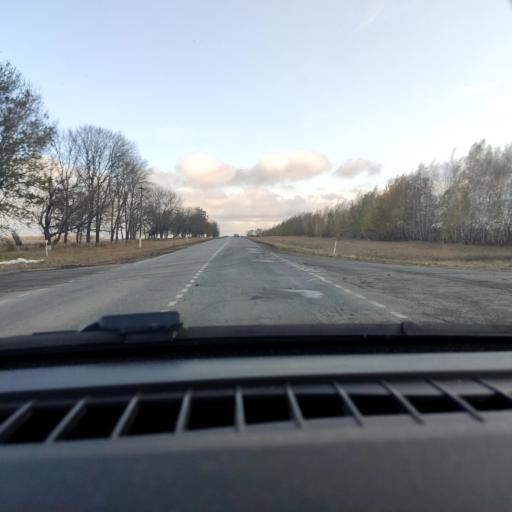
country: RU
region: Belgorod
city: Ilovka
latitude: 50.7134
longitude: 38.6635
